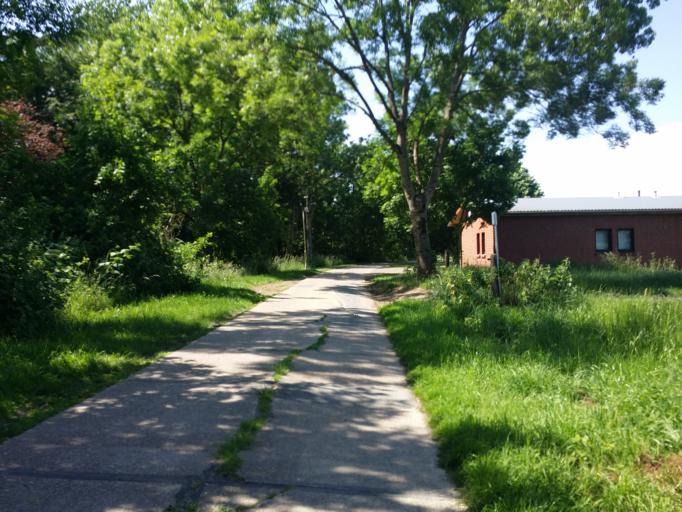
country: DE
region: Lower Saxony
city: Lemwerder
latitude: 53.1436
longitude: 8.5676
